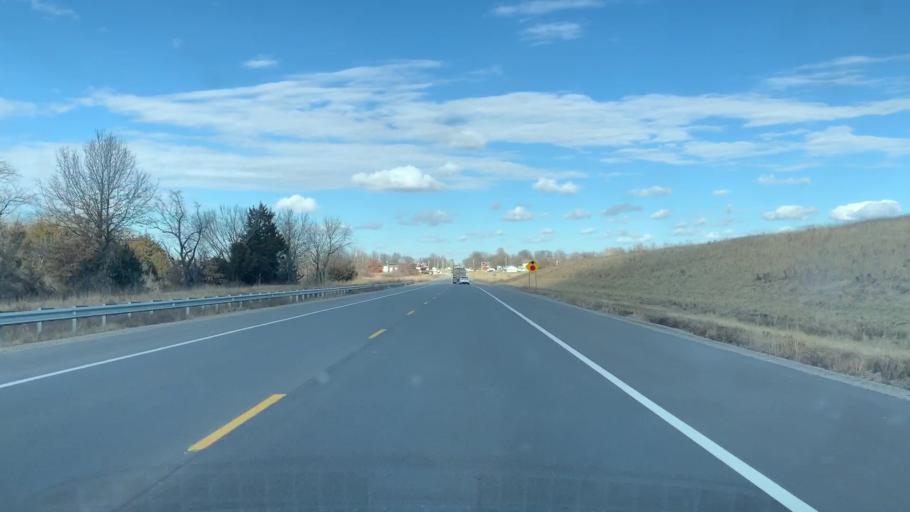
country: US
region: Kansas
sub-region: Crawford County
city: Pittsburg
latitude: 37.3345
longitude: -94.8321
